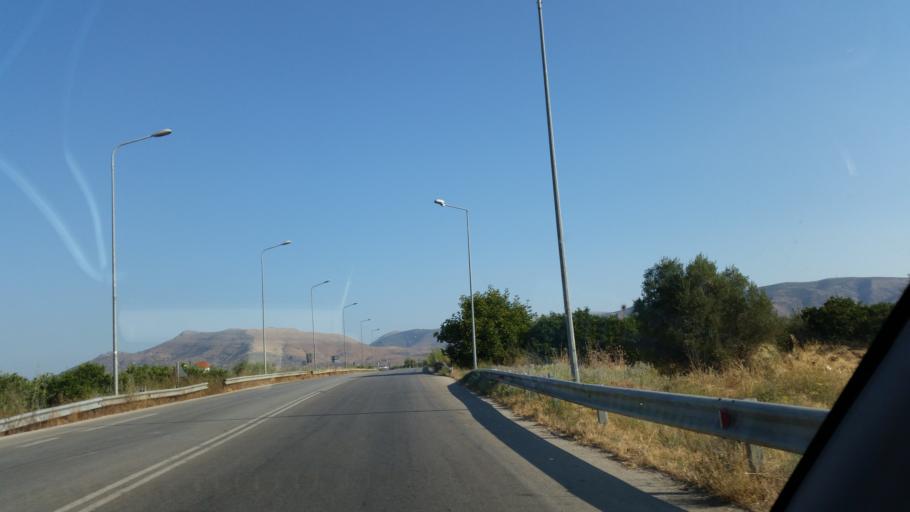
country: GR
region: Peloponnese
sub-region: Nomos Argolidos
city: Ayia Trias
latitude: 37.6338
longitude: 22.8172
